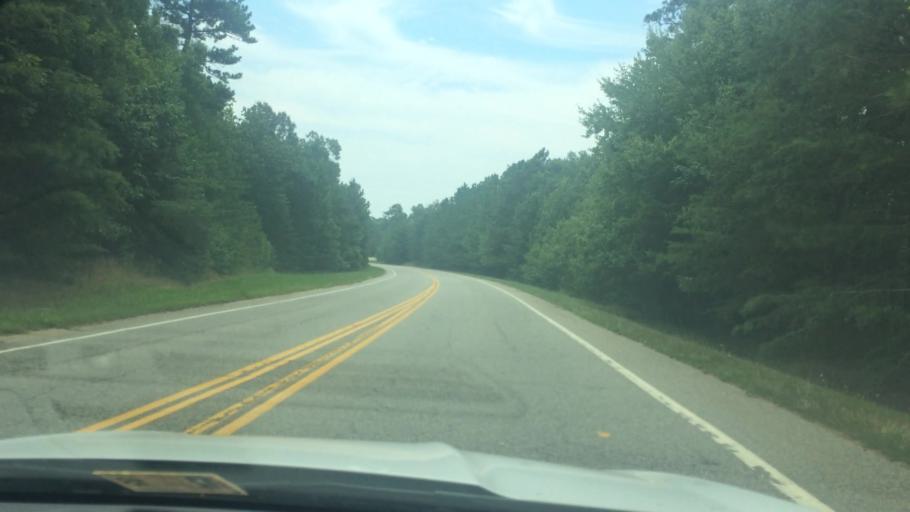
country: US
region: Virginia
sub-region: James City County
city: Williamsburg
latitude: 37.2702
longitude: -76.8077
